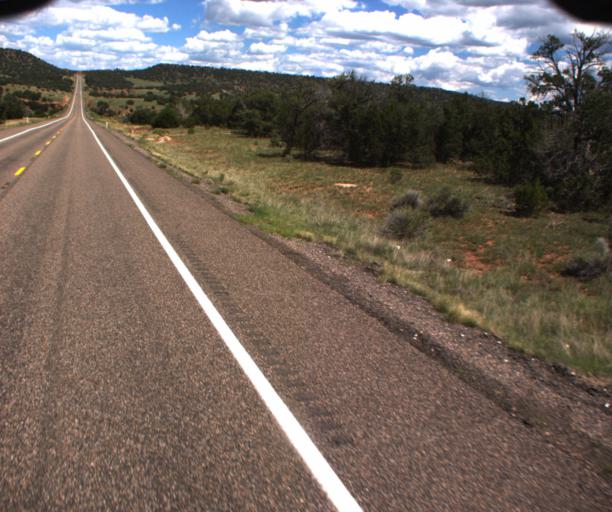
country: US
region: Arizona
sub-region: Apache County
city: Springerville
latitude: 34.1614
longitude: -109.0802
